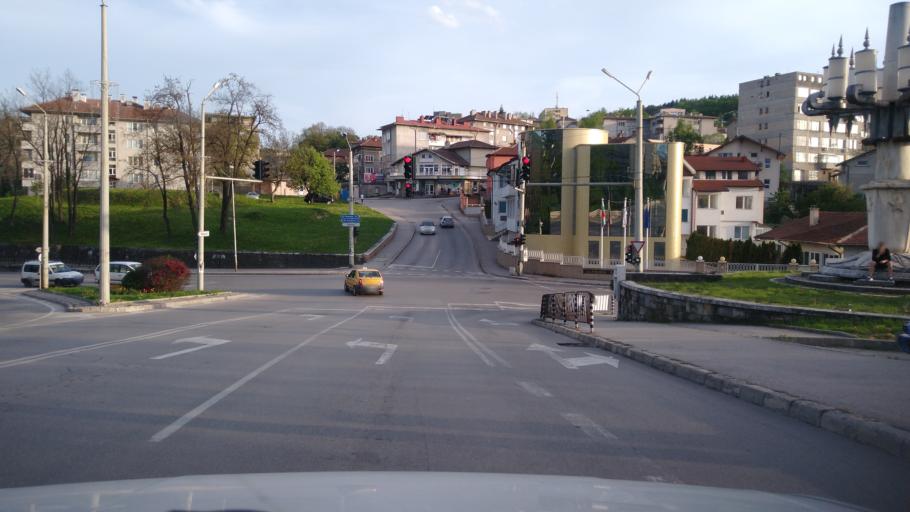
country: BG
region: Gabrovo
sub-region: Obshtina Gabrovo
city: Gabrovo
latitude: 42.8807
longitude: 25.3126
